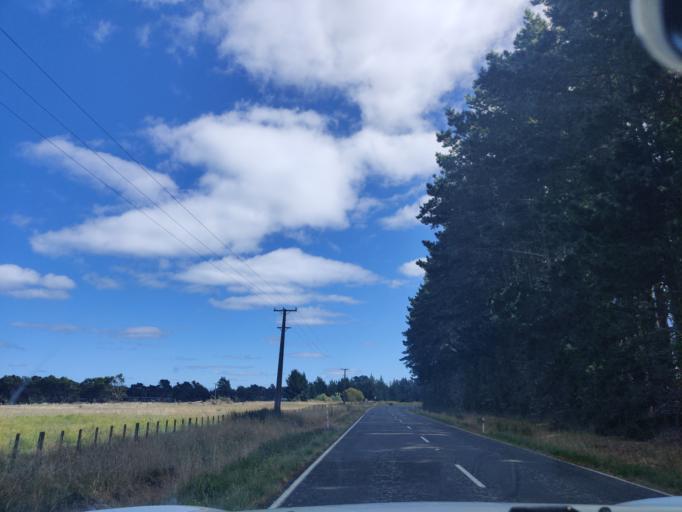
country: NZ
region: Manawatu-Wanganui
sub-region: Horowhenua District
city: Foxton
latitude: -40.3809
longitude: 175.2611
